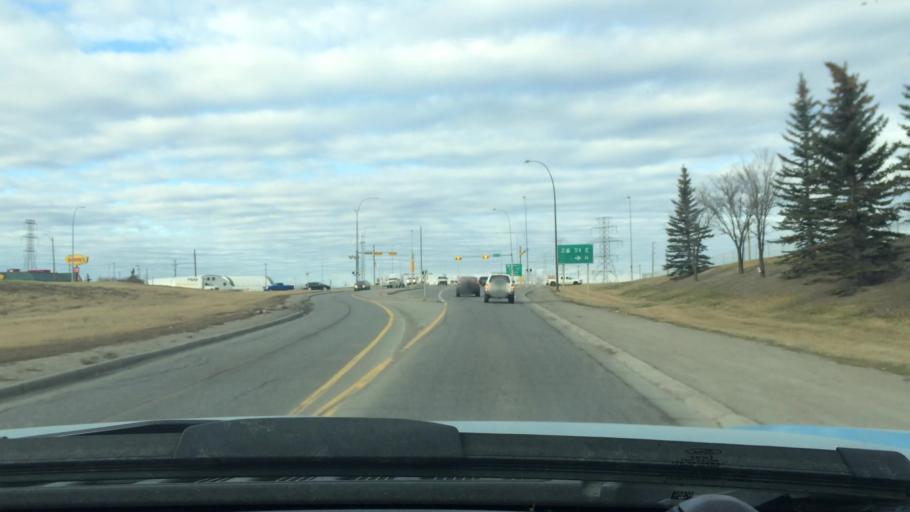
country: CA
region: Alberta
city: Calgary
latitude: 51.0155
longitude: -113.9967
